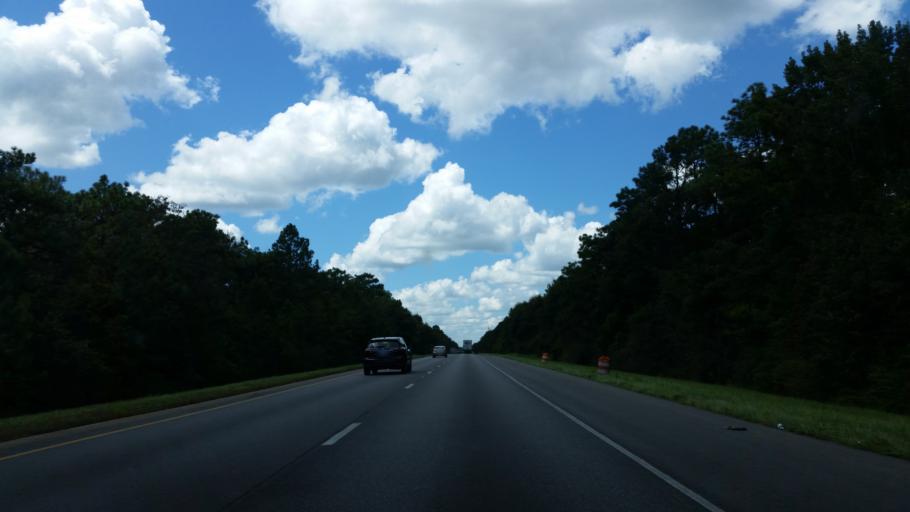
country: US
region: Alabama
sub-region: Baldwin County
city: Loxley
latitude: 30.6568
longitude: -87.8065
